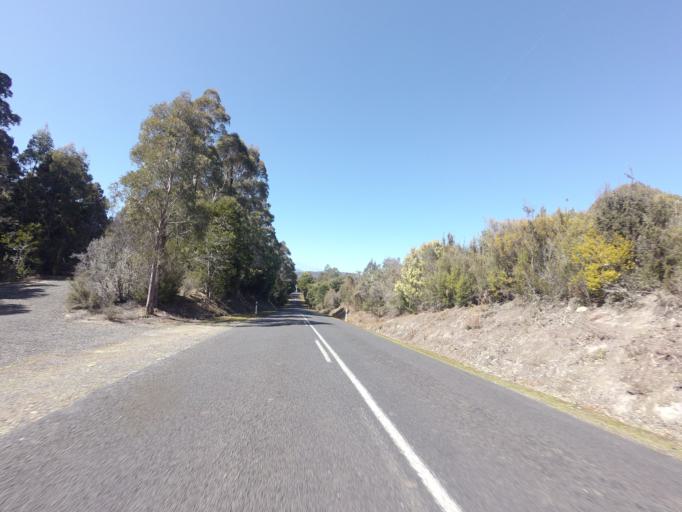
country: AU
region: Tasmania
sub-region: Derwent Valley
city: New Norfolk
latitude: -42.7591
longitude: 146.5299
